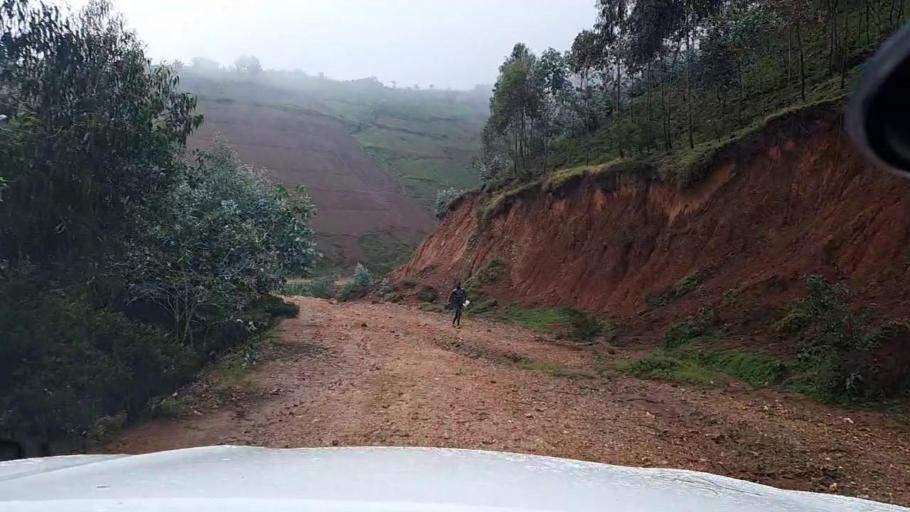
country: RW
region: Western Province
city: Kibuye
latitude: -2.1422
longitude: 29.4585
